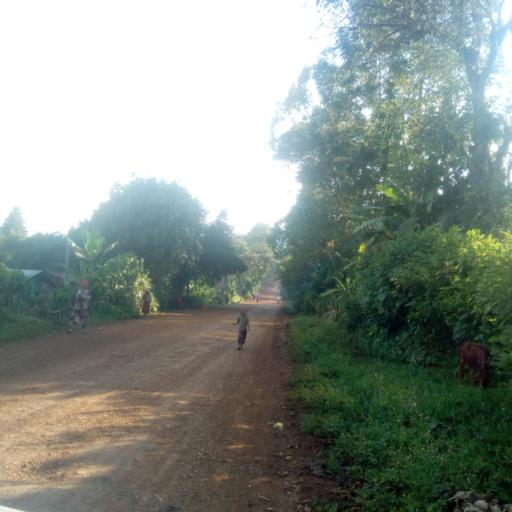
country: ET
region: Oromiya
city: Gore
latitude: 7.8325
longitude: 35.4678
